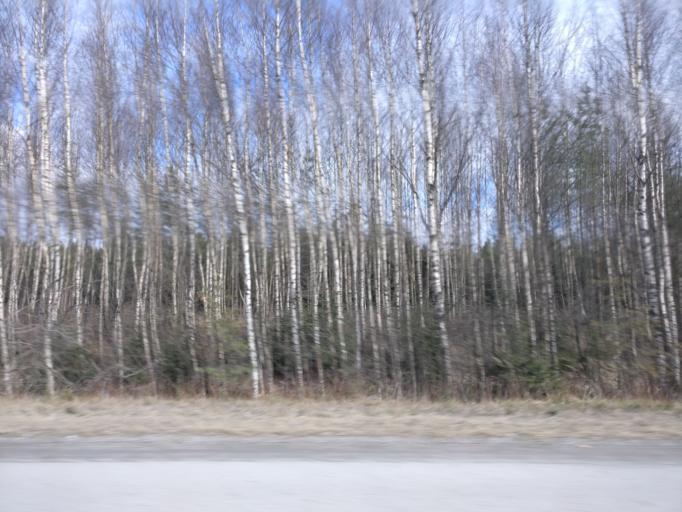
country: FI
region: Haeme
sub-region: Haemeenlinna
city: Janakkala
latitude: 60.9216
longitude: 24.5284
